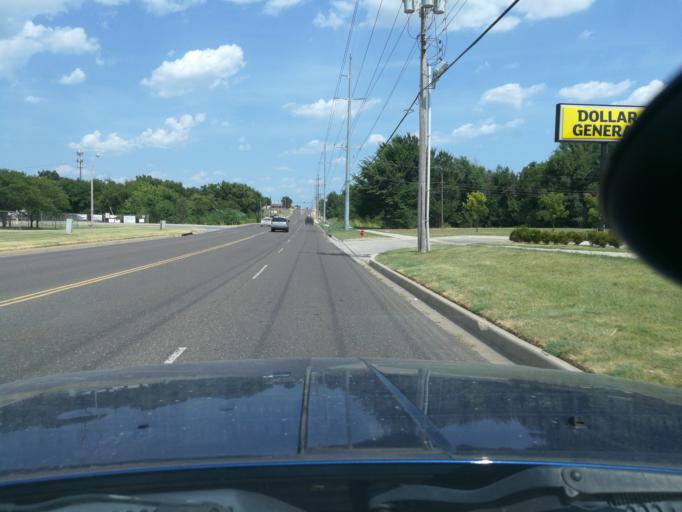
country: US
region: Oklahoma
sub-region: Oklahoma County
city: Del City
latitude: 35.4208
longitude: -97.4833
